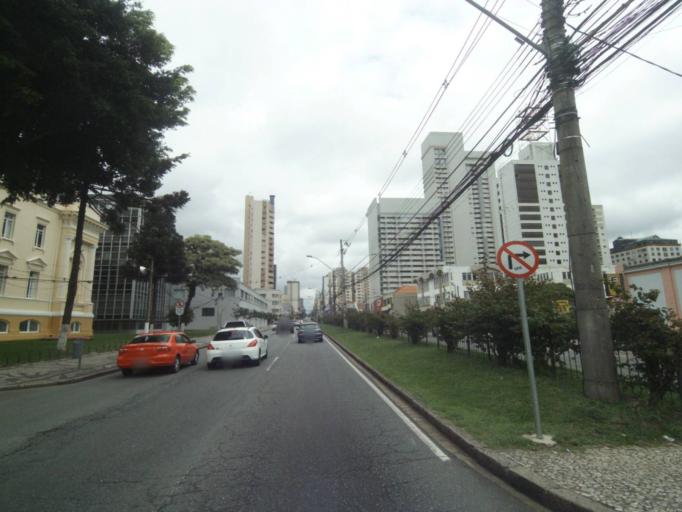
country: BR
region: Parana
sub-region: Curitiba
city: Curitiba
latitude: -25.4360
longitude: -49.2666
